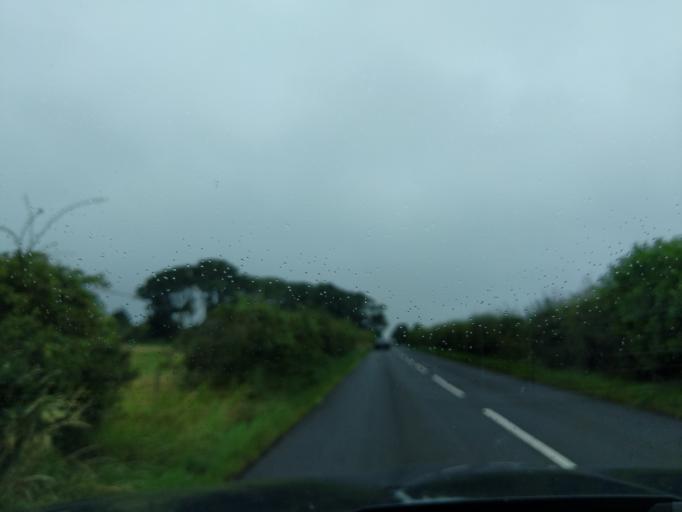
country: GB
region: England
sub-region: Northumberland
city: Lowick
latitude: 55.6550
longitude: -1.9106
